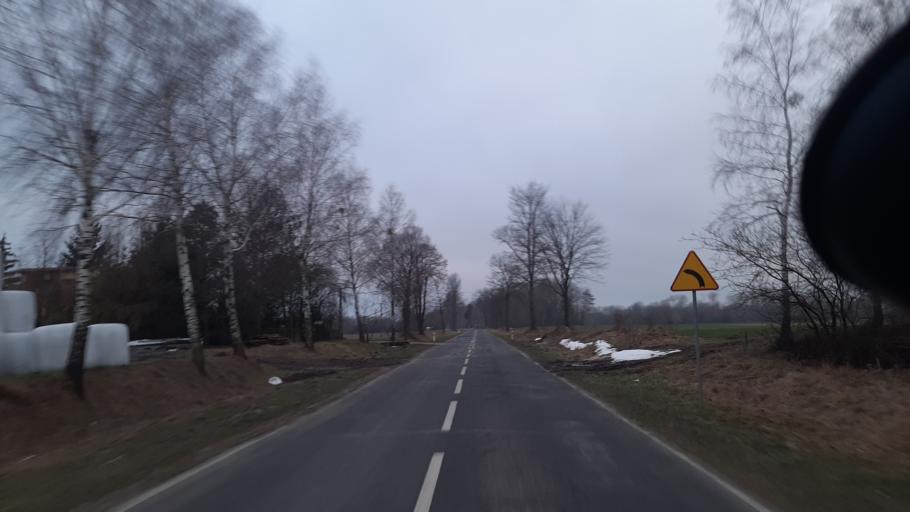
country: PL
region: Lublin Voivodeship
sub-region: Powiat parczewski
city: Podedworze
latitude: 51.5953
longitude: 23.1657
